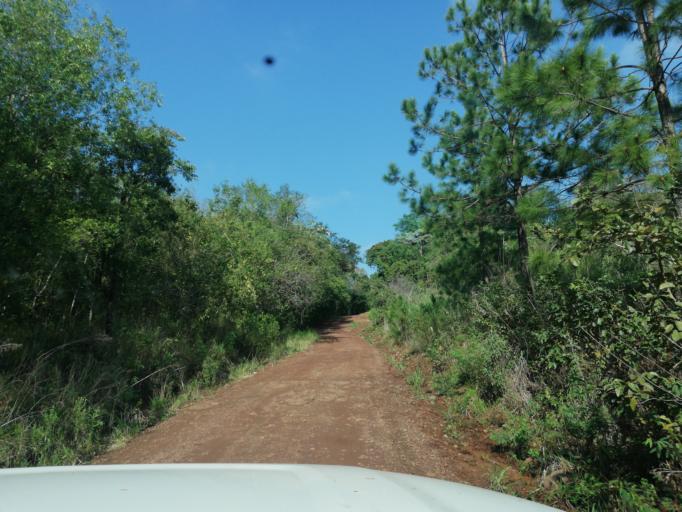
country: AR
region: Misiones
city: Cerro Azul
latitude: -27.6178
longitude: -55.5232
